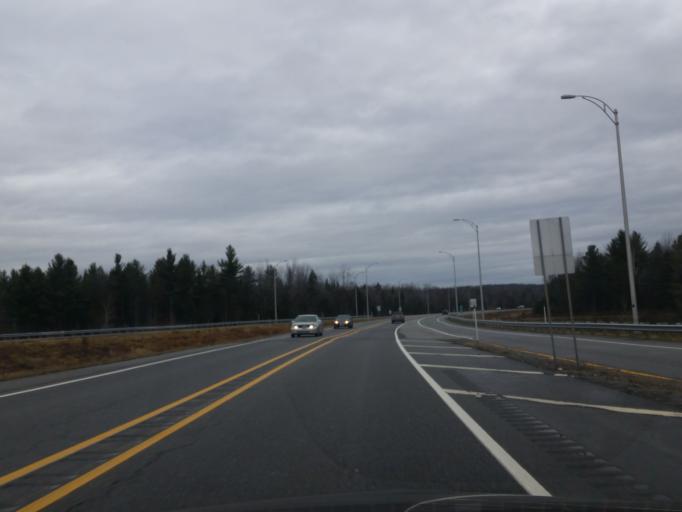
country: CA
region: Ontario
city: Clarence-Rockland
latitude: 45.6106
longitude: -75.3873
